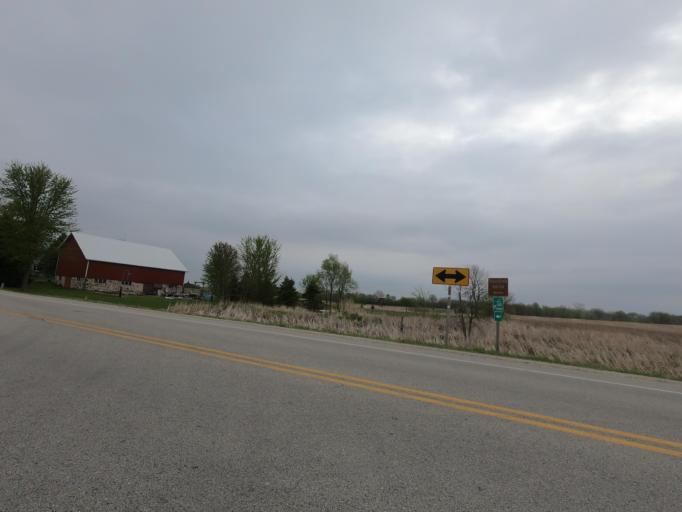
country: US
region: Wisconsin
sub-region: Jefferson County
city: Jefferson
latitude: 43.0319
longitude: -88.7736
